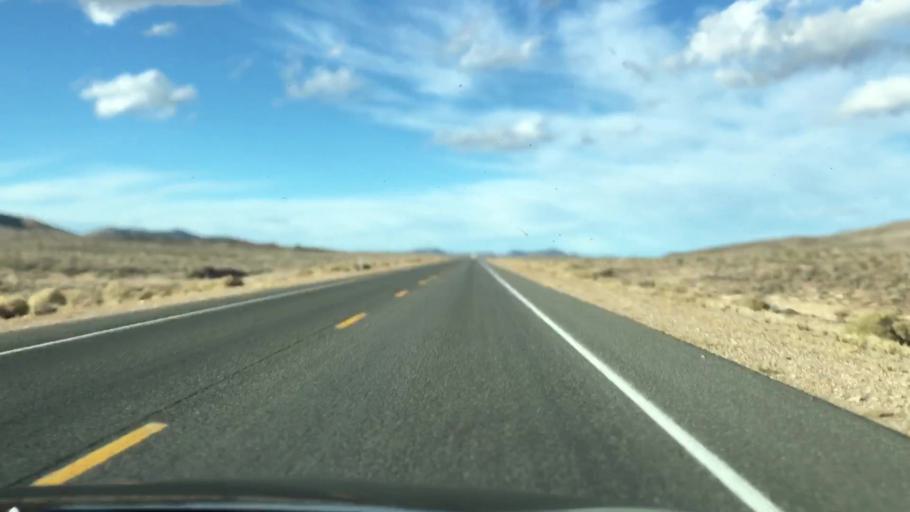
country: US
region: Nevada
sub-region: Esmeralda County
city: Goldfield
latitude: 37.5320
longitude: -117.1929
